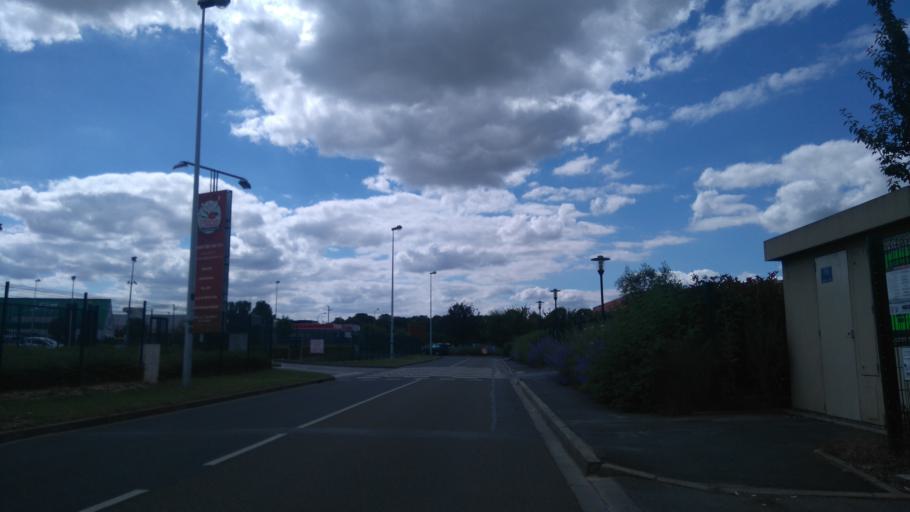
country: FR
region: Picardie
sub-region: Departement de l'Oise
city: Creil
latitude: 49.2442
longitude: 2.4722
